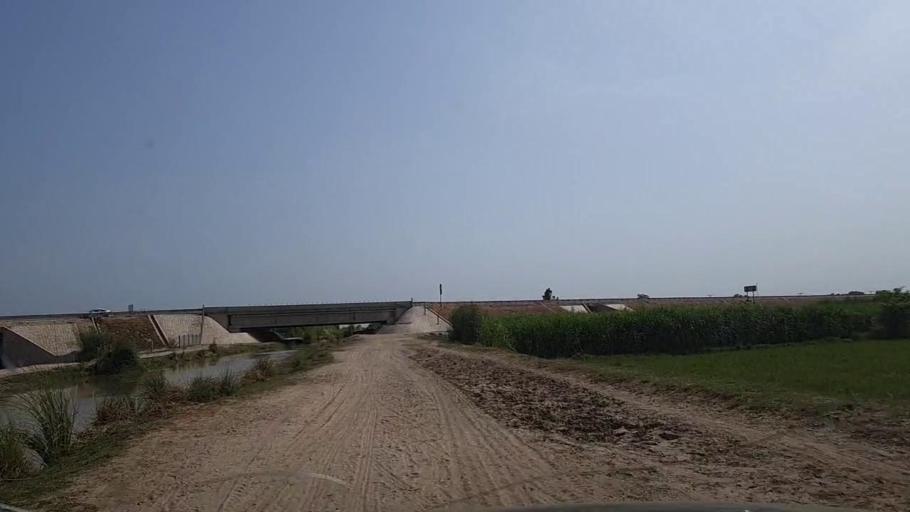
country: PK
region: Sindh
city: Ghotki
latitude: 28.0640
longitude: 69.3826
